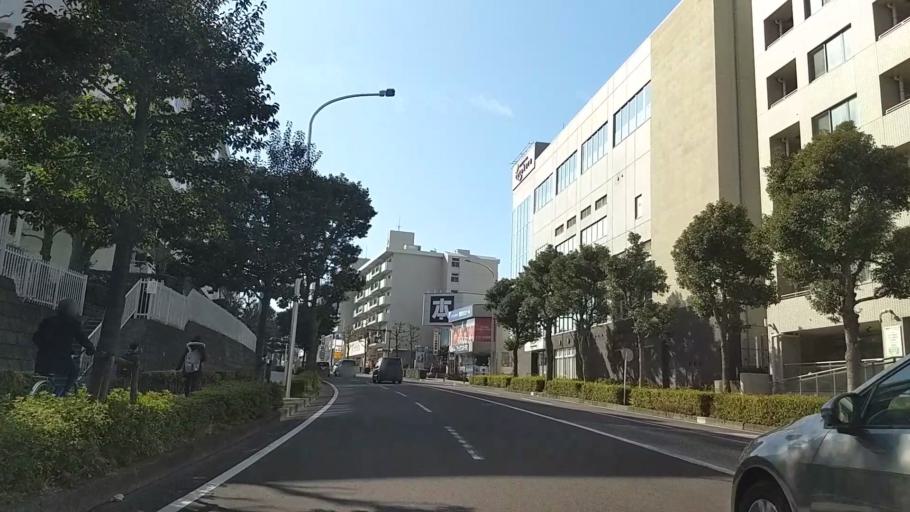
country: JP
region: Kanagawa
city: Kamakura
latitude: 35.3772
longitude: 139.5758
